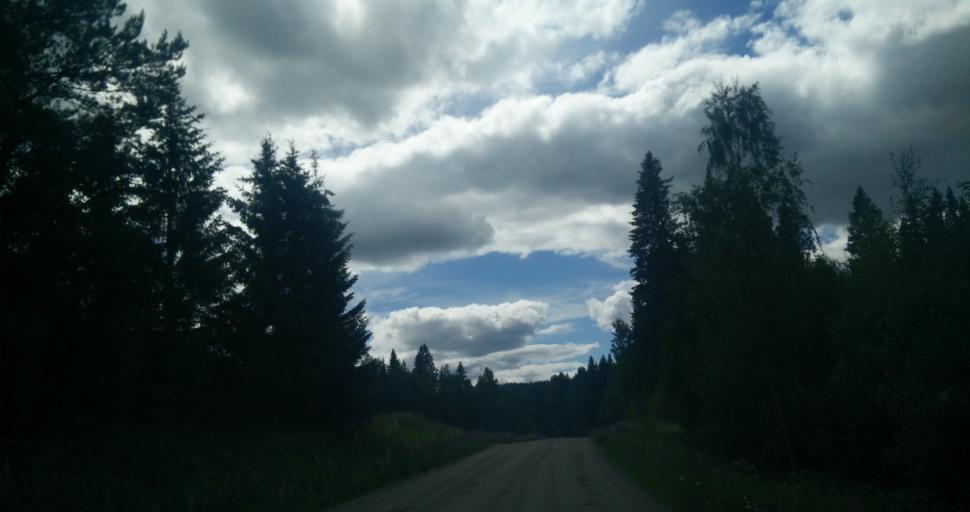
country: SE
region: Gaevleborg
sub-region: Nordanstigs Kommun
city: Bergsjoe
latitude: 62.1186
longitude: 17.1003
